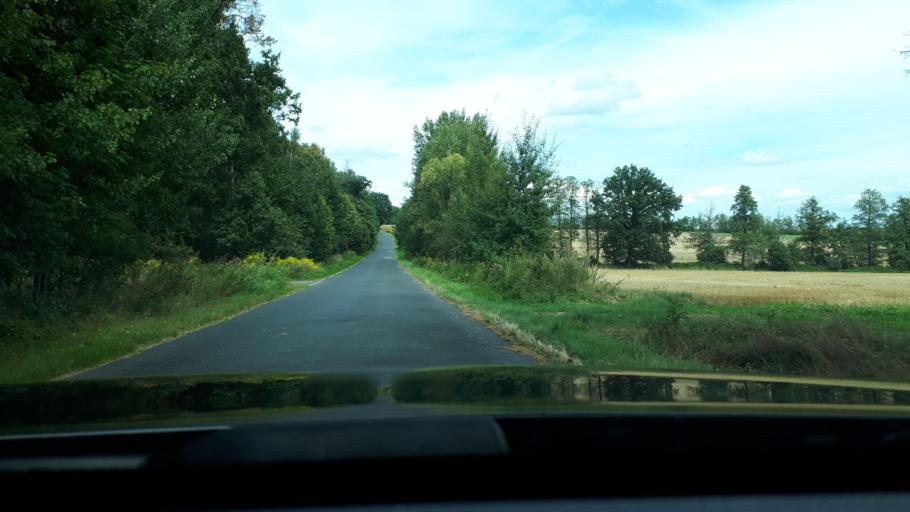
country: PL
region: Lower Silesian Voivodeship
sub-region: Powiat zlotoryjski
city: Olszanica
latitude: 51.1908
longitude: 15.7789
